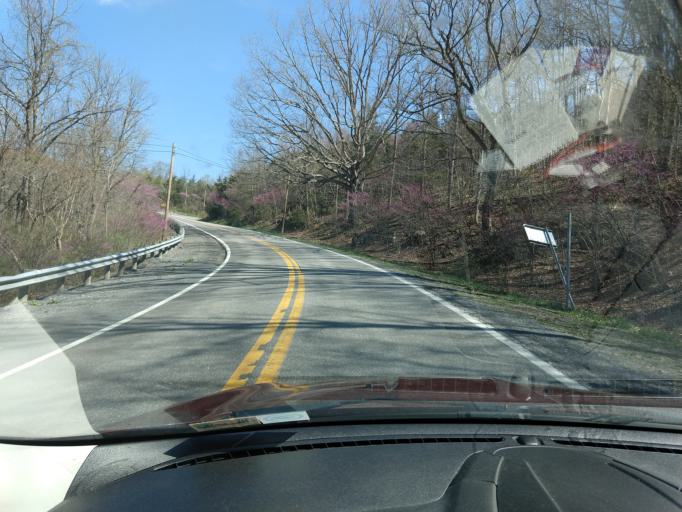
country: US
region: West Virginia
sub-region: Greenbrier County
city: Ronceverte
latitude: 37.7545
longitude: -80.5338
